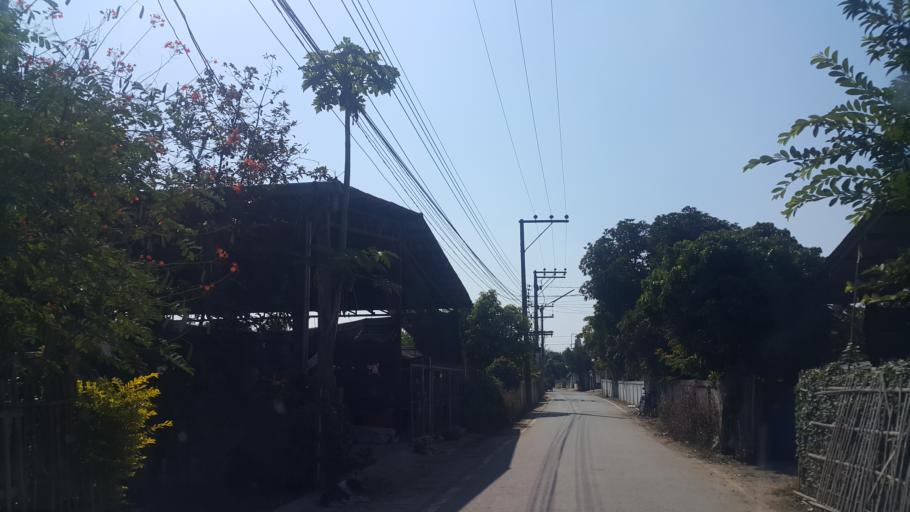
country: TH
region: Chiang Mai
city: San Kamphaeng
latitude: 18.6986
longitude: 99.1641
